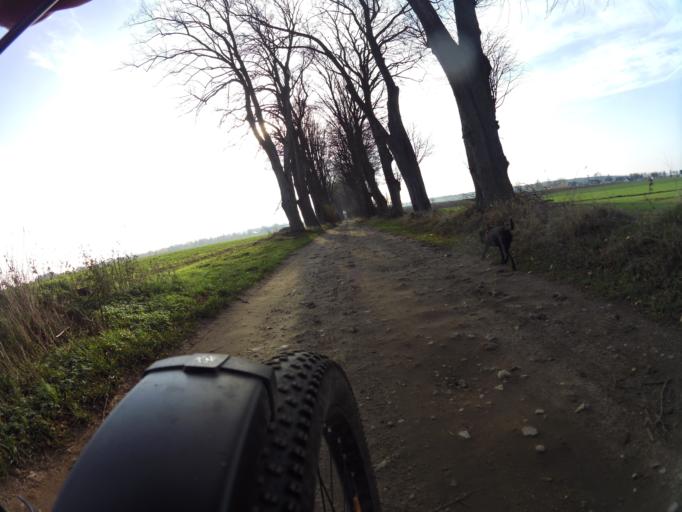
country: PL
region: Pomeranian Voivodeship
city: Strzelno
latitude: 54.7551
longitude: 18.2912
